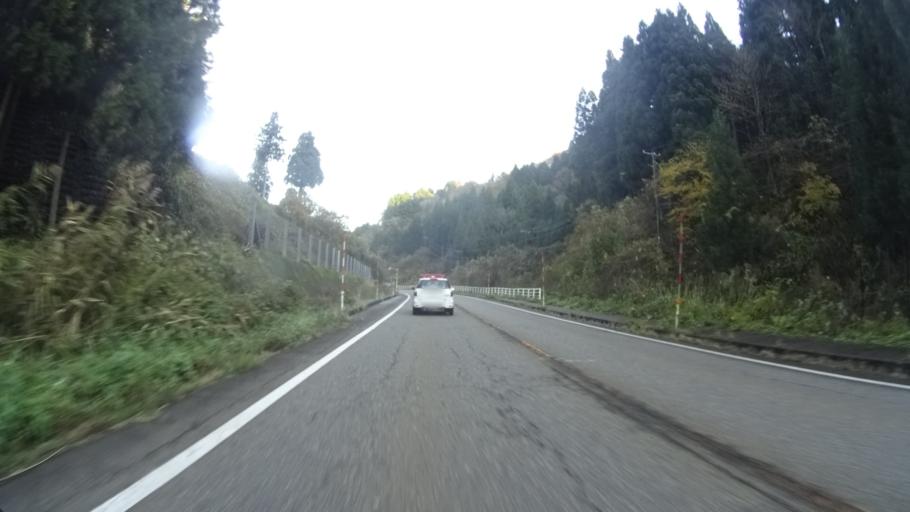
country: JP
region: Niigata
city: Kashiwazaki
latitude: 37.4123
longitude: 138.6763
